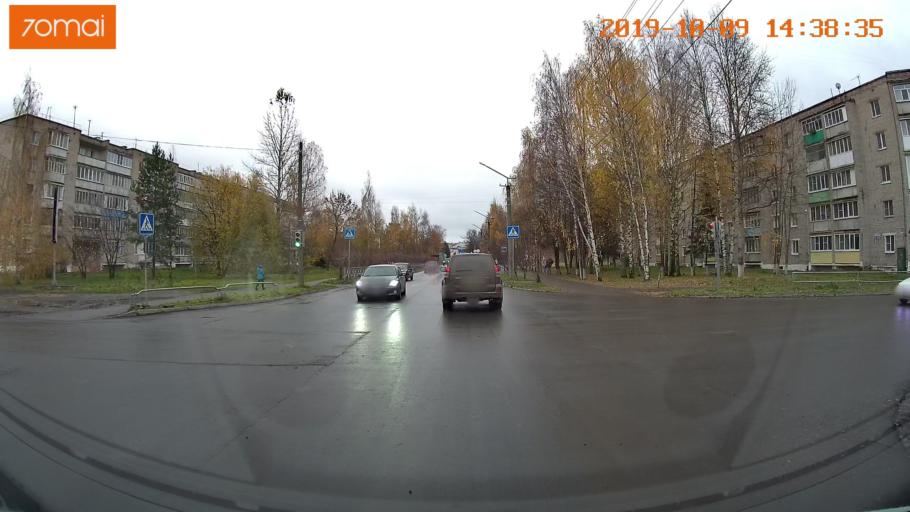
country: RU
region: Kostroma
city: Buy
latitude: 58.4796
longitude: 41.5357
